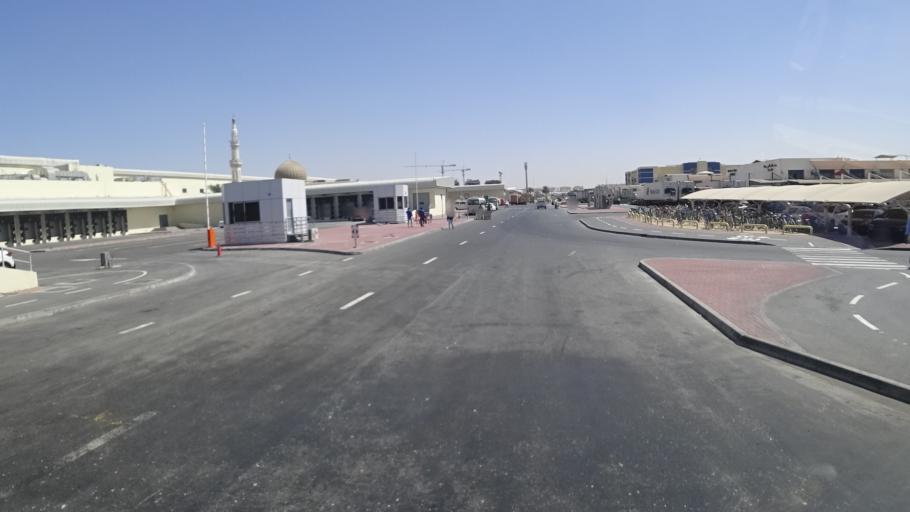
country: AE
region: Ash Shariqah
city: Sharjah
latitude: 25.1754
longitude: 55.3889
